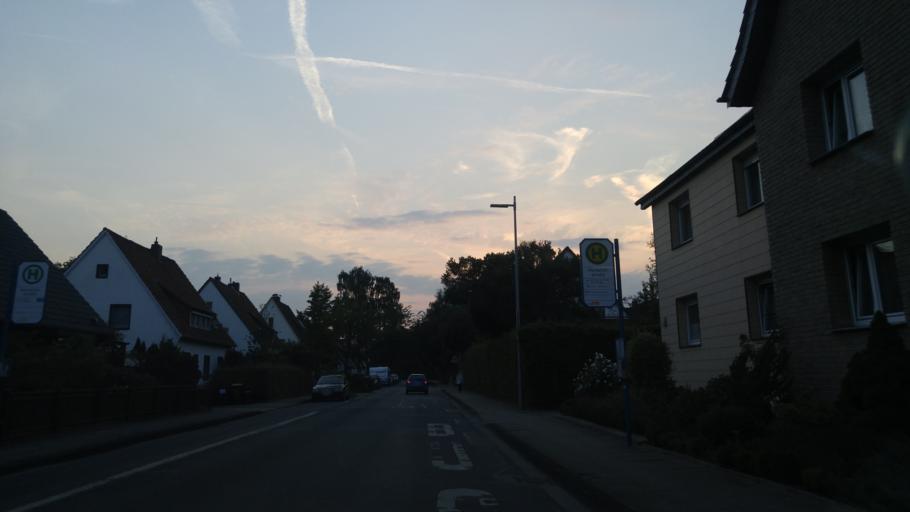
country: DE
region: North Rhine-Westphalia
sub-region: Regierungsbezirk Detmold
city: Bielefeld
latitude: 52.0548
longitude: 8.5237
